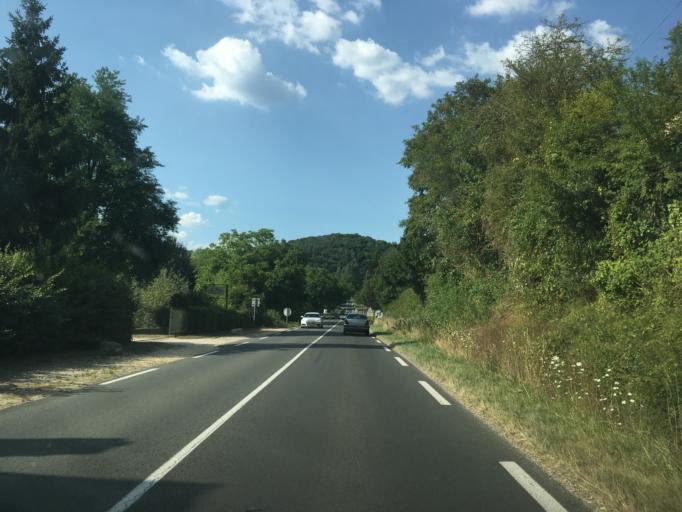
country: FR
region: Aquitaine
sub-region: Departement de la Dordogne
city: Cenac-et-Saint-Julien
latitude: 44.8406
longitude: 1.1709
